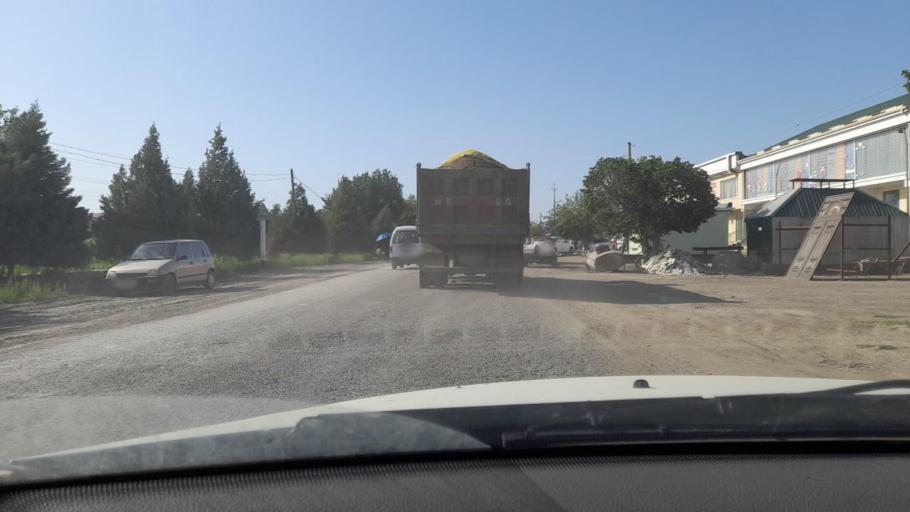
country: UZ
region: Bukhara
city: Romiton
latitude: 40.0475
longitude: 64.3287
